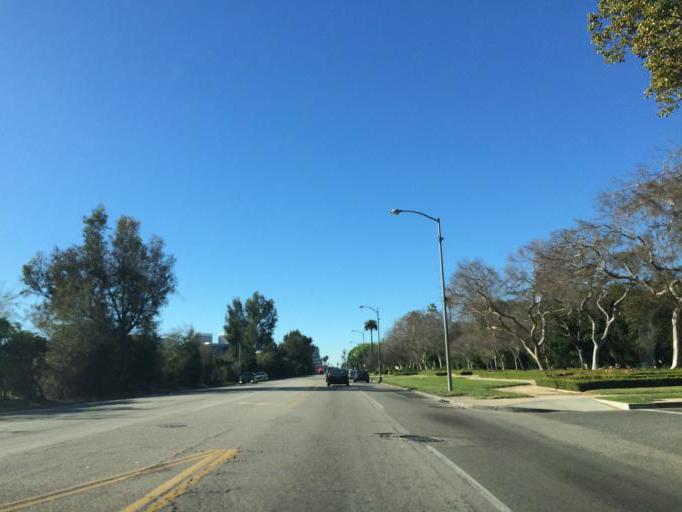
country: US
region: California
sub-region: Los Angeles County
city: Beverly Hills
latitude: 34.0767
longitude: -118.3964
